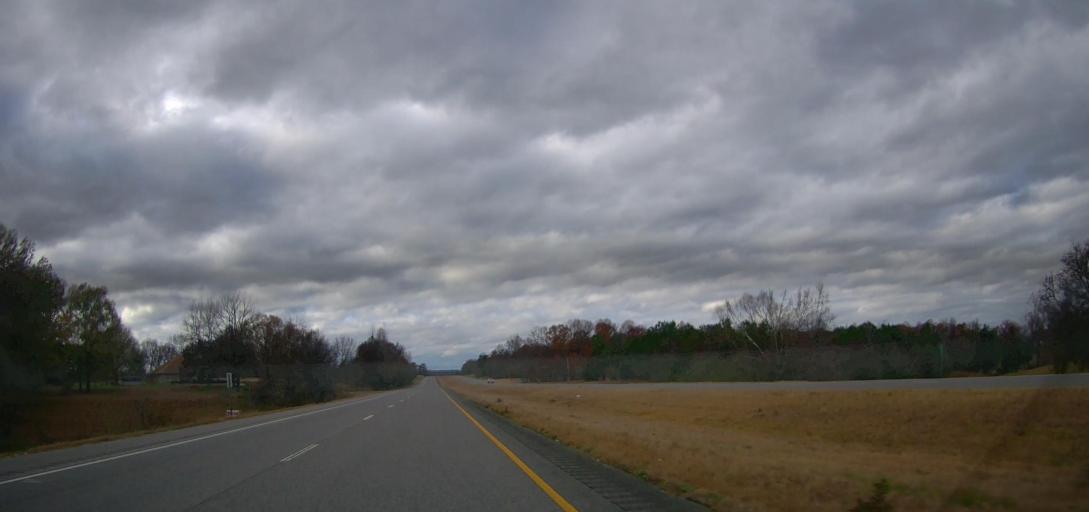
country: US
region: Alabama
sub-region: Lawrence County
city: Town Creek
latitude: 34.5942
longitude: -87.4331
